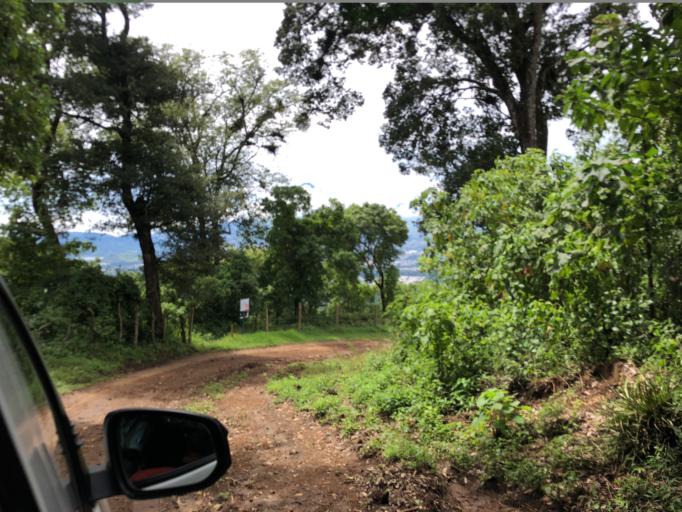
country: GT
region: Guatemala
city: Santa Catarina Pinula
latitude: 14.5326
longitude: -90.4974
